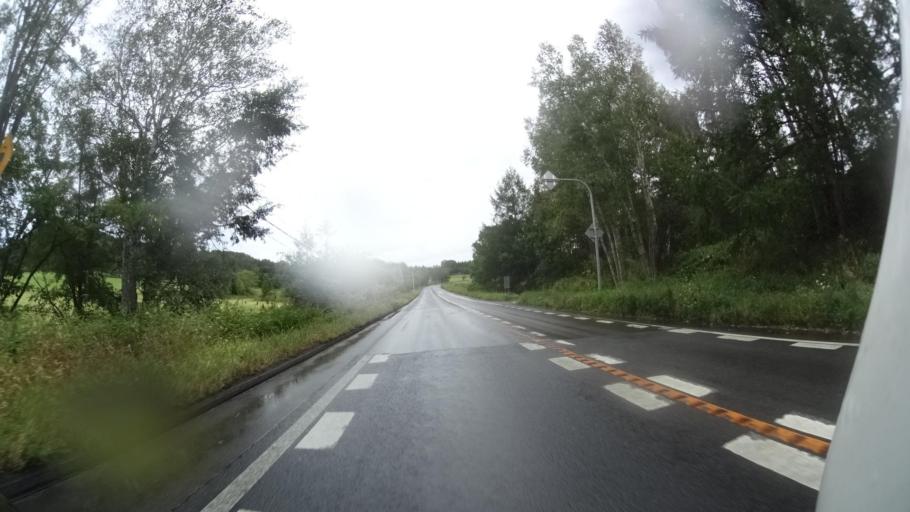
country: JP
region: Hokkaido
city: Kitami
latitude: 44.0954
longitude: 143.7387
